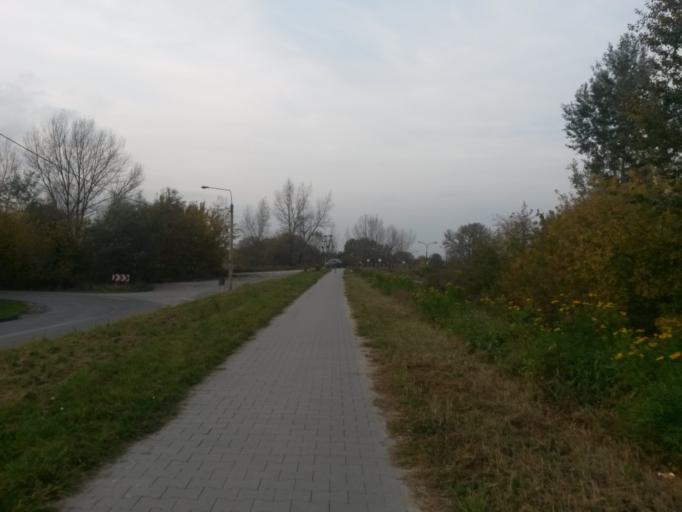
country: PL
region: Masovian Voivodeship
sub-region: Warszawa
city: Wilanow
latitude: 52.1897
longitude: 21.1036
